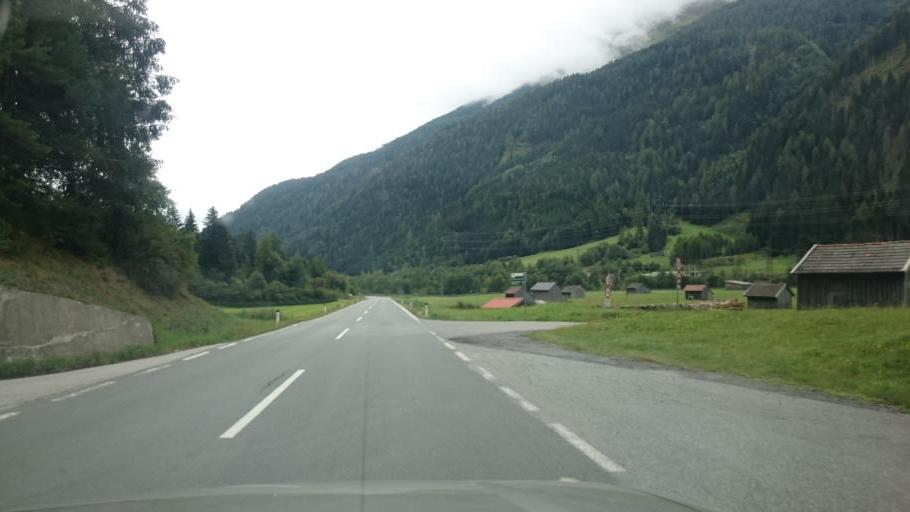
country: AT
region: Tyrol
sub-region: Politischer Bezirk Landeck
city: Flirsch
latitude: 47.1519
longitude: 10.3595
